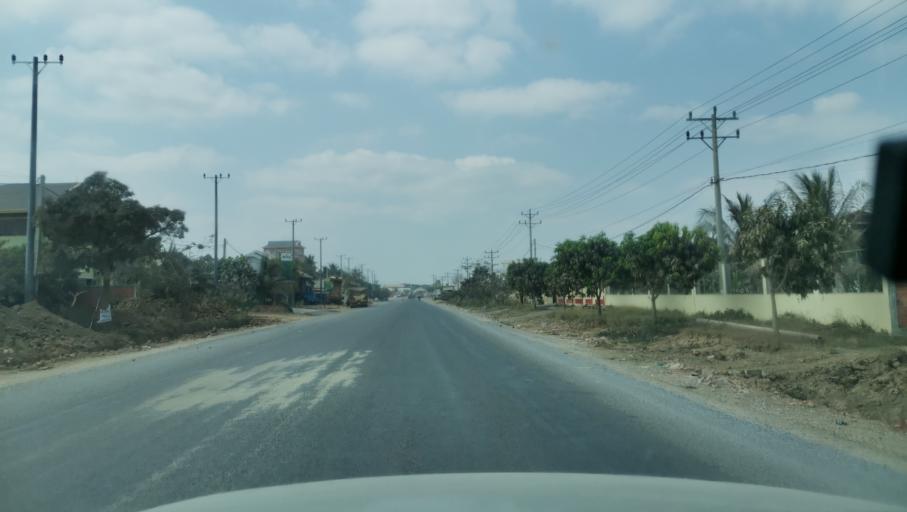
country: KH
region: Battambang
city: Battambang
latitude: 13.0759
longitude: 103.1835
